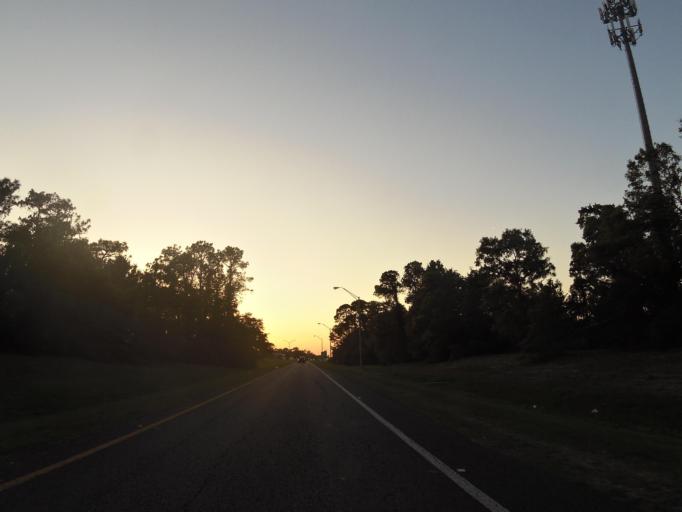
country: US
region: Florida
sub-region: Duval County
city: Jacksonville
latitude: 30.3420
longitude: -81.5418
